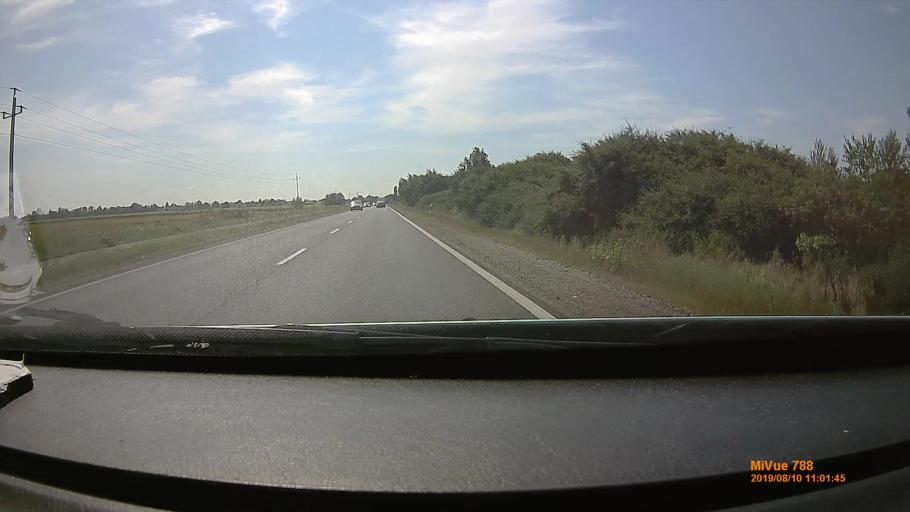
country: HU
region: Borsod-Abauj-Zemplen
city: Malyi
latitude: 48.0059
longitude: 20.8287
